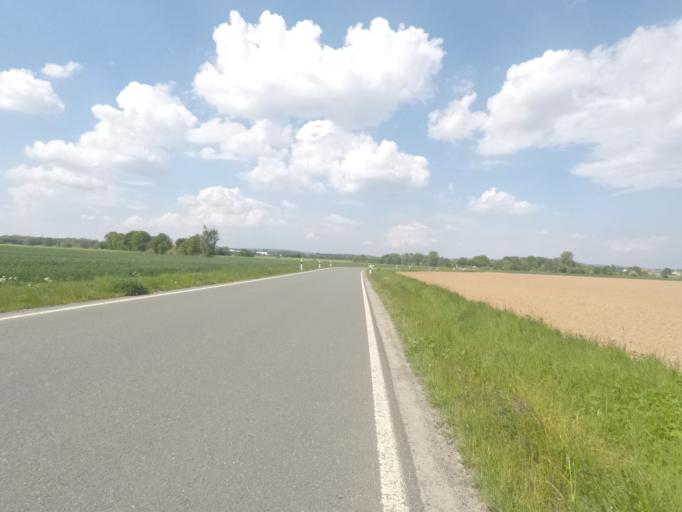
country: DE
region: North Rhine-Westphalia
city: Spenge
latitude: 52.1838
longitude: 8.5116
